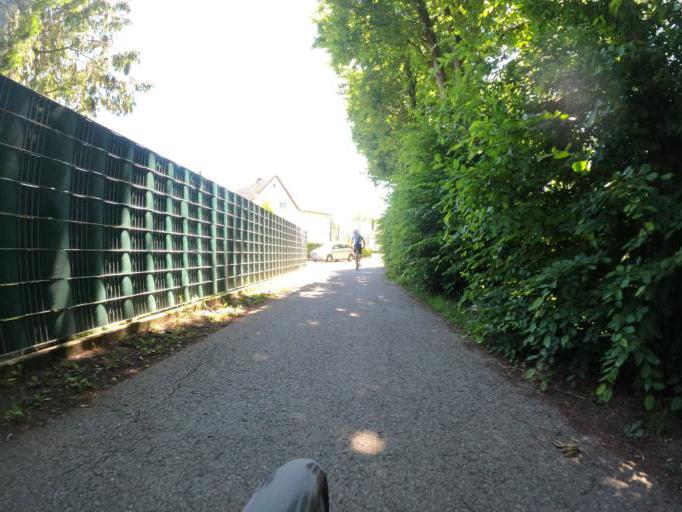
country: DE
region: Baden-Wuerttemberg
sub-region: Regierungsbezirk Stuttgart
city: Vaihingen an der Enz
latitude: 48.9537
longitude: 8.9663
